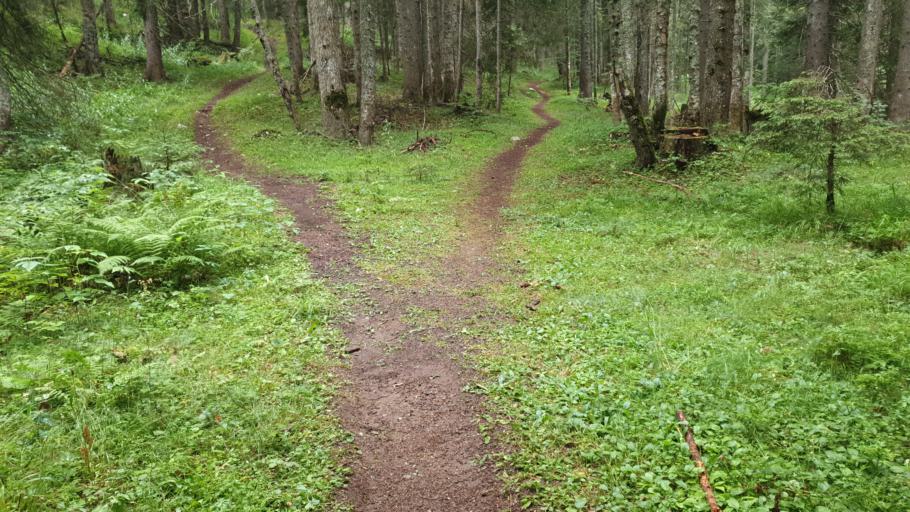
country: ME
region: Opstina Zabljak
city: Zabljak
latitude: 43.1475
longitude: 19.1047
